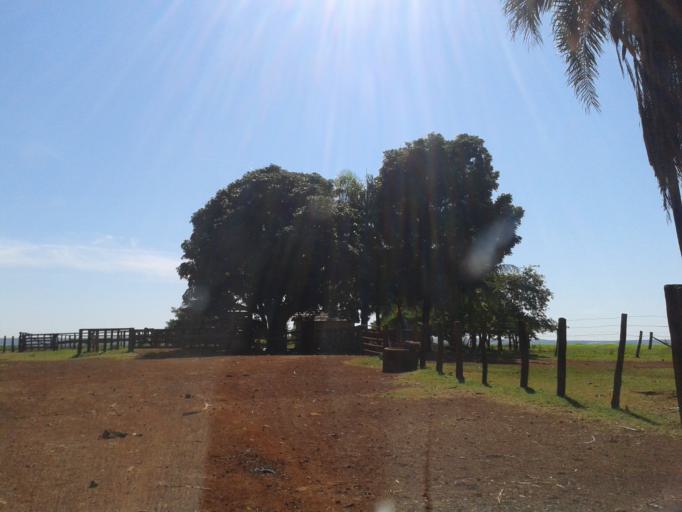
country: BR
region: Minas Gerais
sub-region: Centralina
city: Centralina
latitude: -18.6523
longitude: -49.2685
